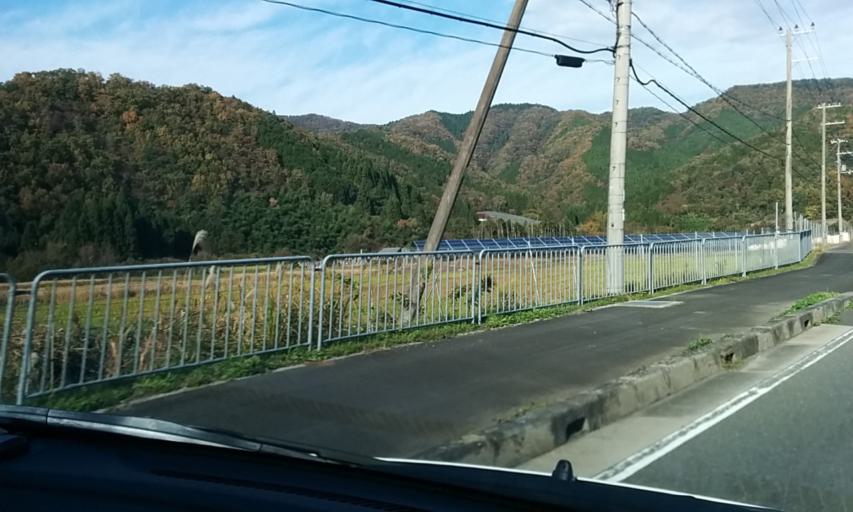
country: JP
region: Kyoto
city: Ayabe
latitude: 35.2062
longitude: 135.2662
